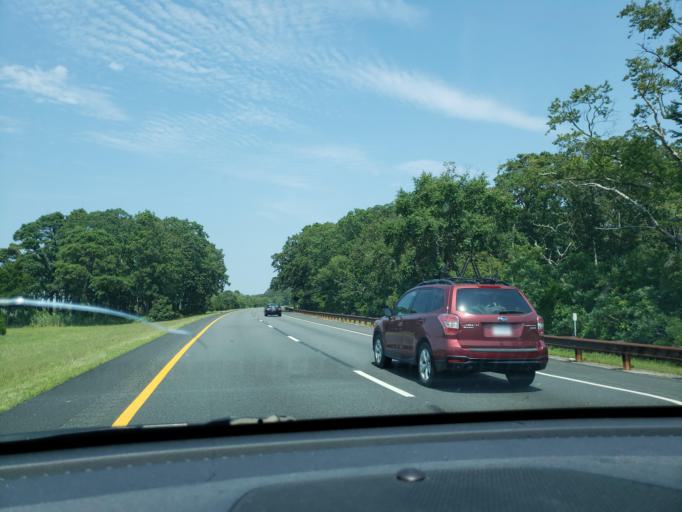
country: US
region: New Jersey
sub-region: Atlantic County
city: Somers Point
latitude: 39.3172
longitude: -74.6206
